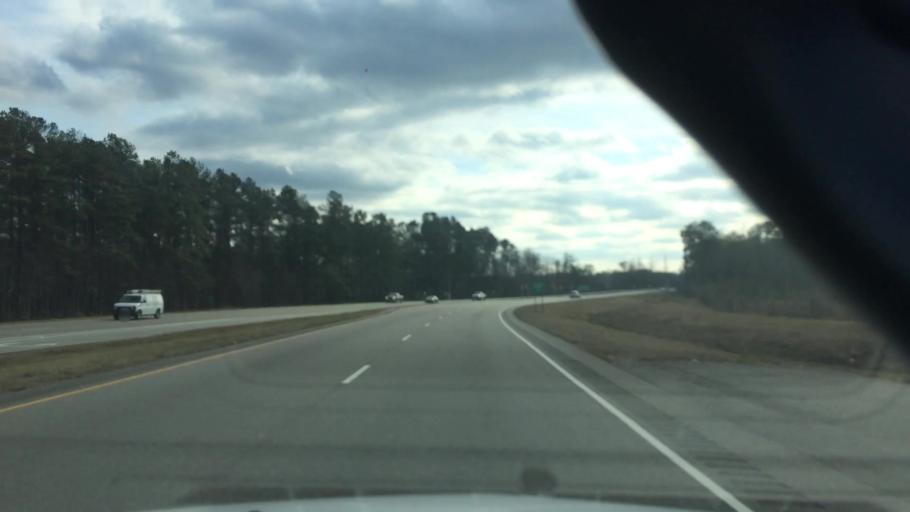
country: US
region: North Carolina
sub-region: Brunswick County
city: Bolivia
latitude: 34.1394
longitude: -78.0942
